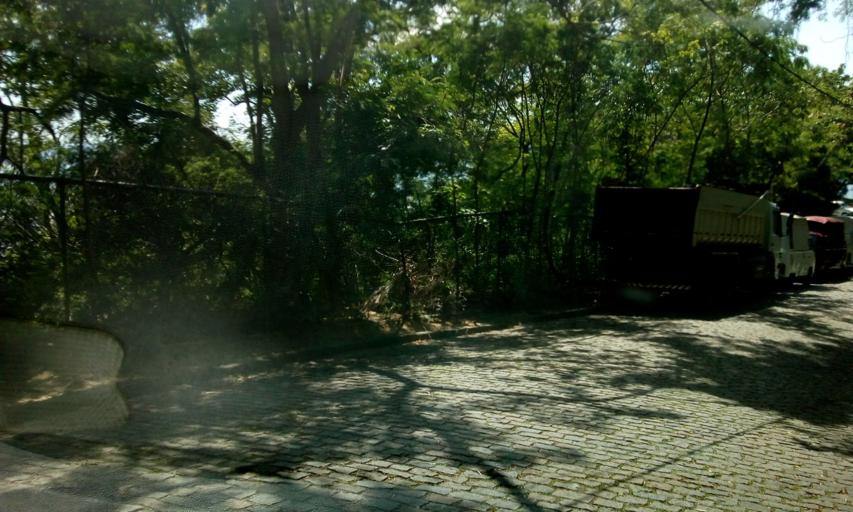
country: BR
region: Rio de Janeiro
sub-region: Rio De Janeiro
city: Rio de Janeiro
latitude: -22.9242
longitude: -43.1848
